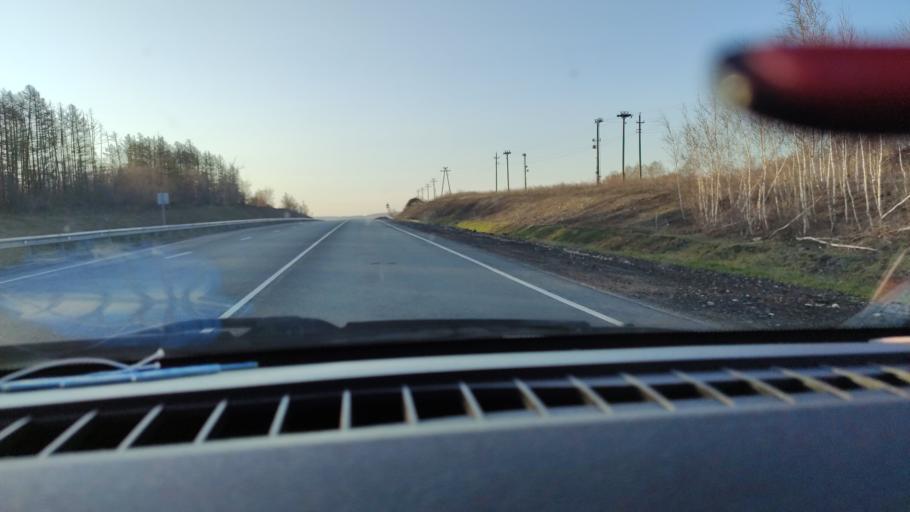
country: RU
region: Saratov
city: Shikhany
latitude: 52.1447
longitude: 47.1992
